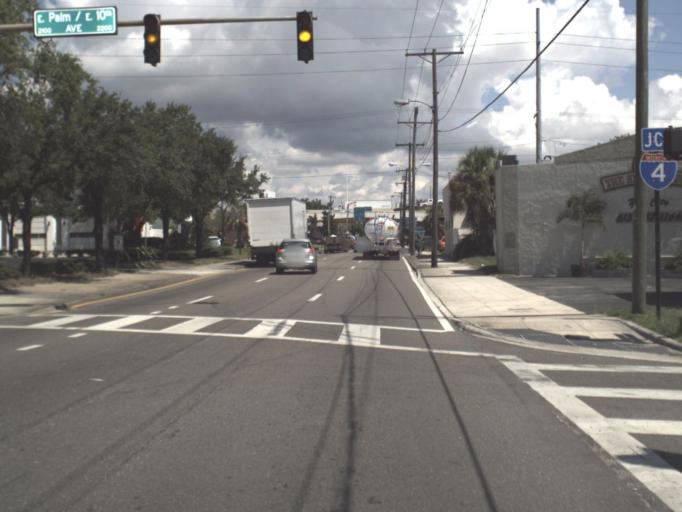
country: US
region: Florida
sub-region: Hillsborough County
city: Tampa
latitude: 27.9624
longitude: -82.4347
